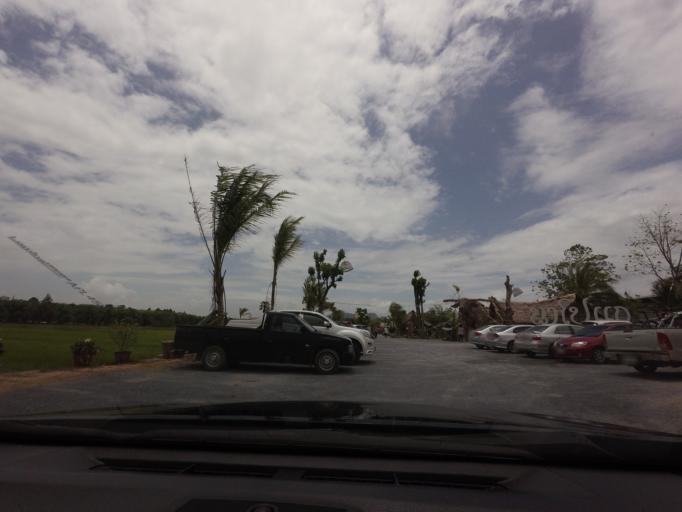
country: TH
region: Phatthalung
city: Khuan Khanun
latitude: 7.7362
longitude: 100.0441
